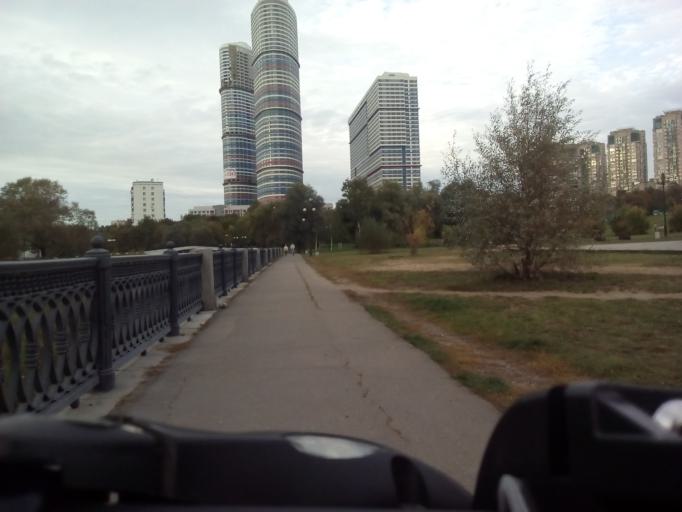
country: RU
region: Moscow
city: Rostokino
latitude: 55.8308
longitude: 37.6541
